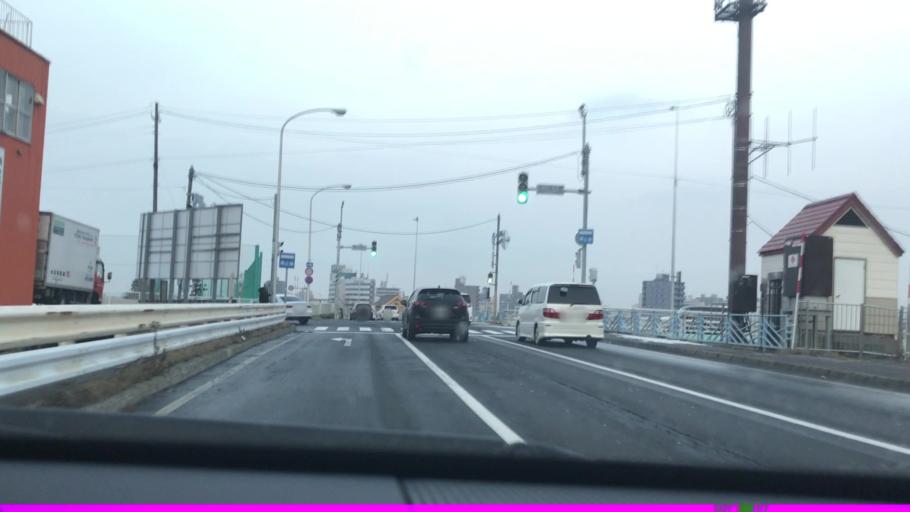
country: JP
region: Hokkaido
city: Sapporo
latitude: 43.0299
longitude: 141.3535
